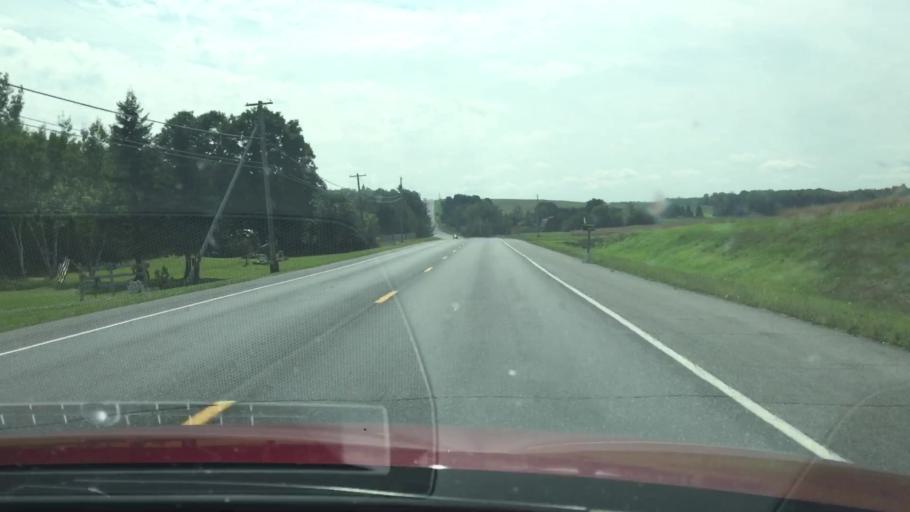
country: US
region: Maine
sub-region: Aroostook County
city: Easton
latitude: 46.5875
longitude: -67.9613
